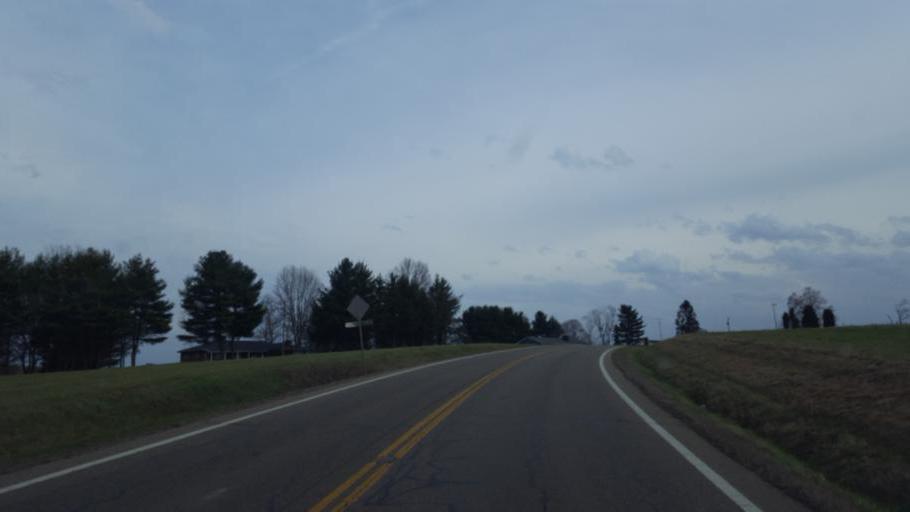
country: US
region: Ohio
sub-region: Coshocton County
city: Coshocton
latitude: 40.2294
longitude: -81.8352
